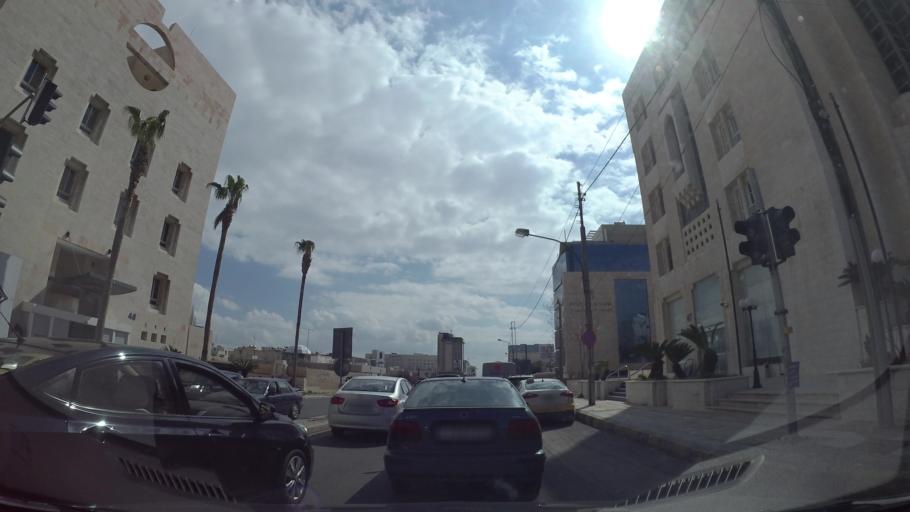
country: JO
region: Amman
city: Amman
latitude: 31.9724
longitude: 35.8968
